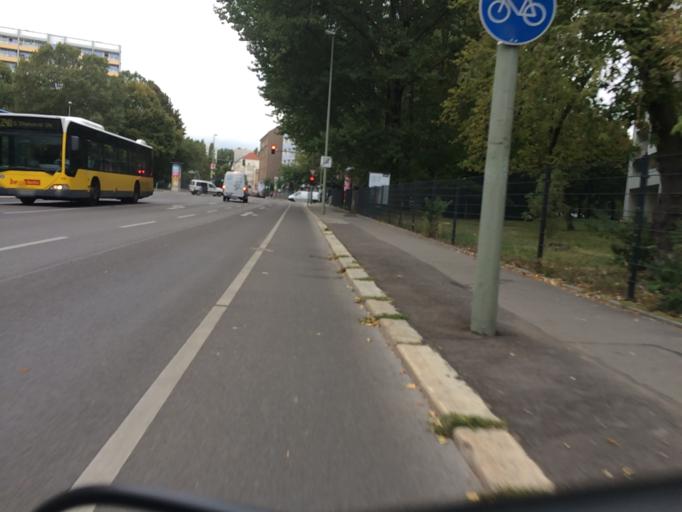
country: DE
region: Berlin
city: Friedrichshain Bezirk
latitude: 52.5134
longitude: 13.4408
